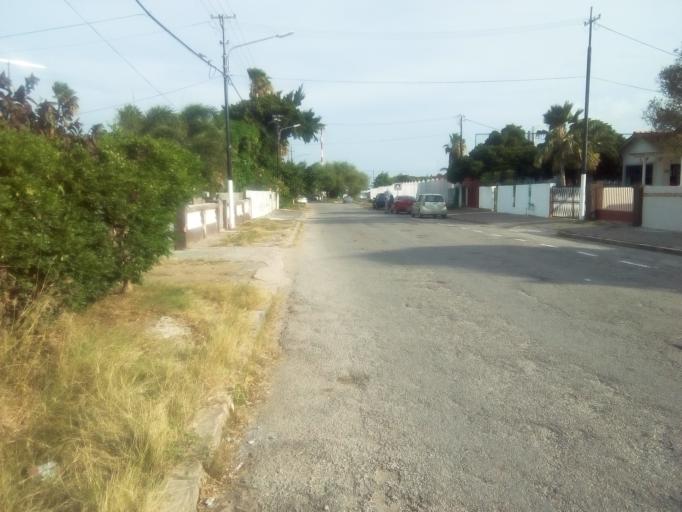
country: CW
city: Willemstad
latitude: 12.1468
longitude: -68.9237
